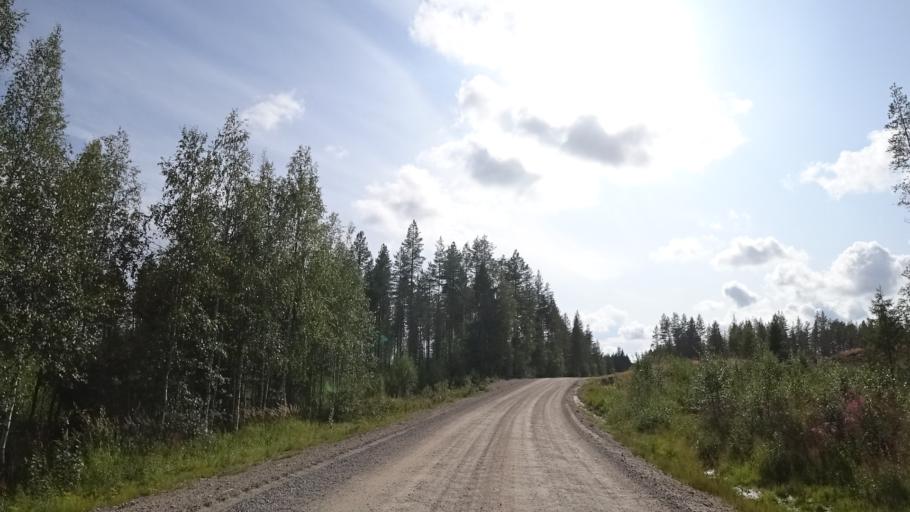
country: FI
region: North Karelia
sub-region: Pielisen Karjala
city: Lieksa
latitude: 63.5770
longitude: 30.1246
